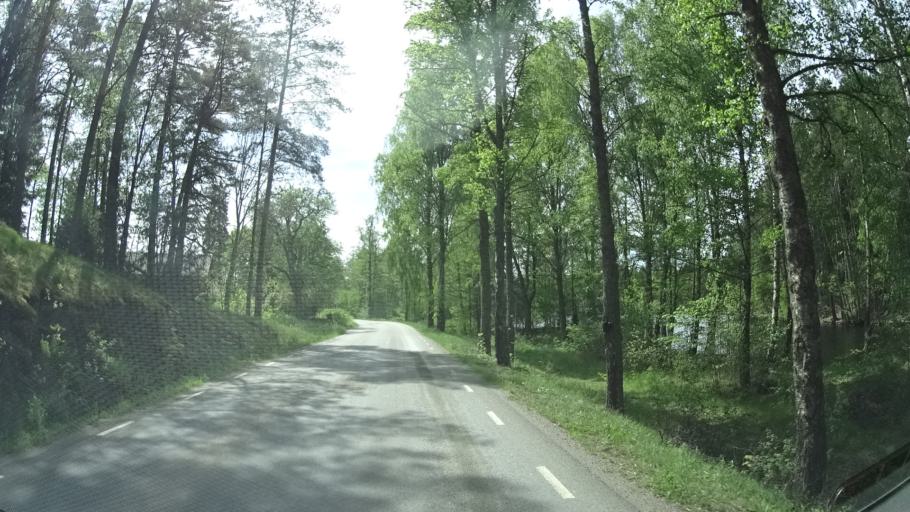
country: SE
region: OEstergoetland
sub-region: Finspangs Kommun
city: Finspang
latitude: 58.7423
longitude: 15.8285
